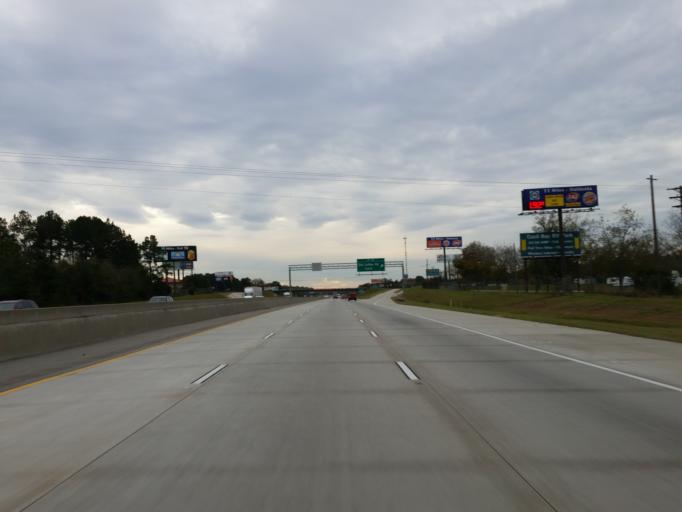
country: US
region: Georgia
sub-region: Lowndes County
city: Hahira
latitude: 31.0490
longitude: -83.3973
